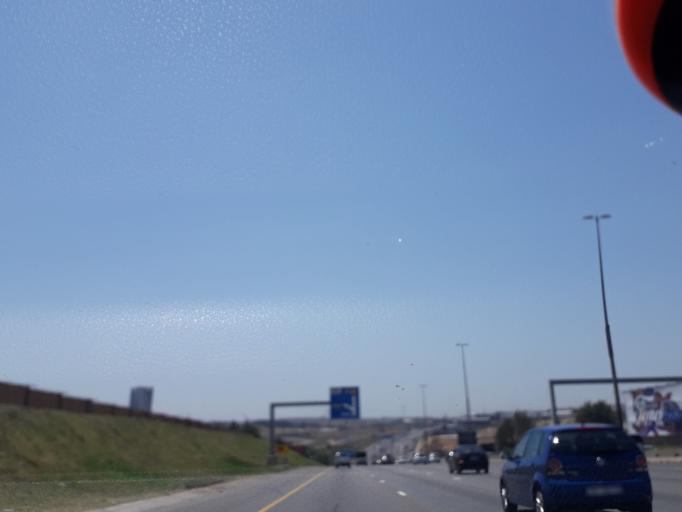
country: ZA
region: Gauteng
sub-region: City of Johannesburg Metropolitan Municipality
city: Midrand
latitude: -26.0364
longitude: 28.1070
